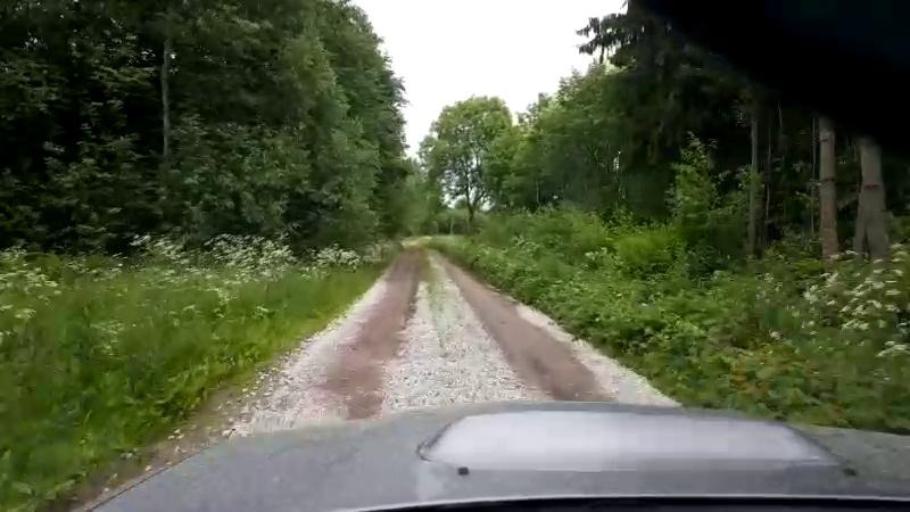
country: EE
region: Paernumaa
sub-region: Tootsi vald
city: Tootsi
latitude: 58.5934
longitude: 24.6632
